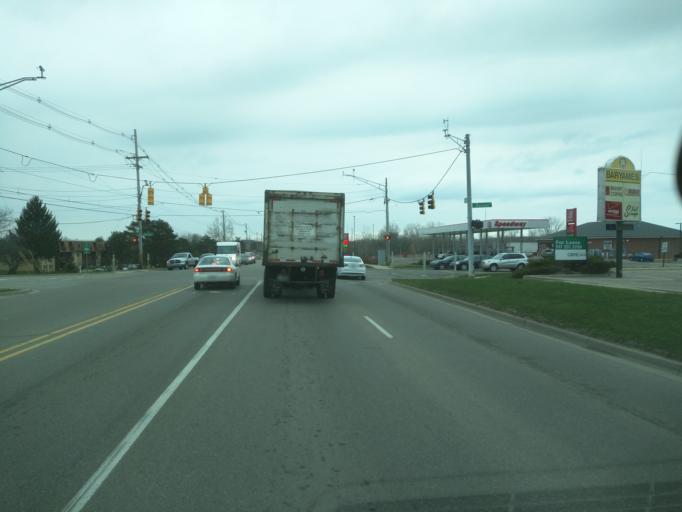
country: US
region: Michigan
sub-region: Ingham County
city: Holt
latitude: 42.6829
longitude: -84.5141
